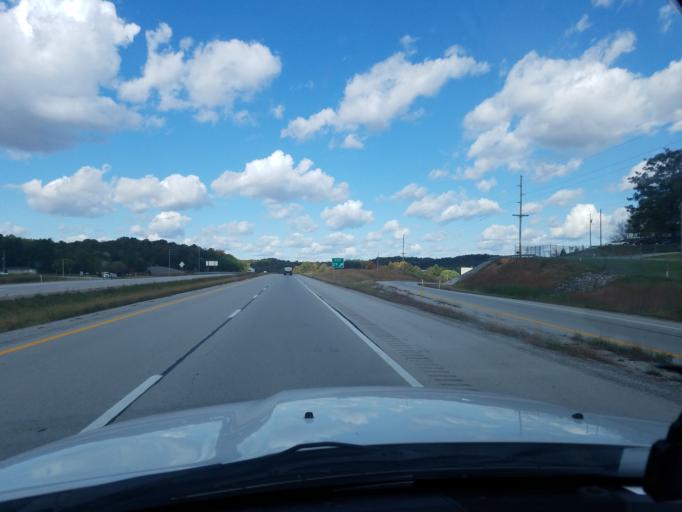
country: US
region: Kentucky
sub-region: Butler County
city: Morgantown
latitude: 37.2119
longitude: -86.7094
